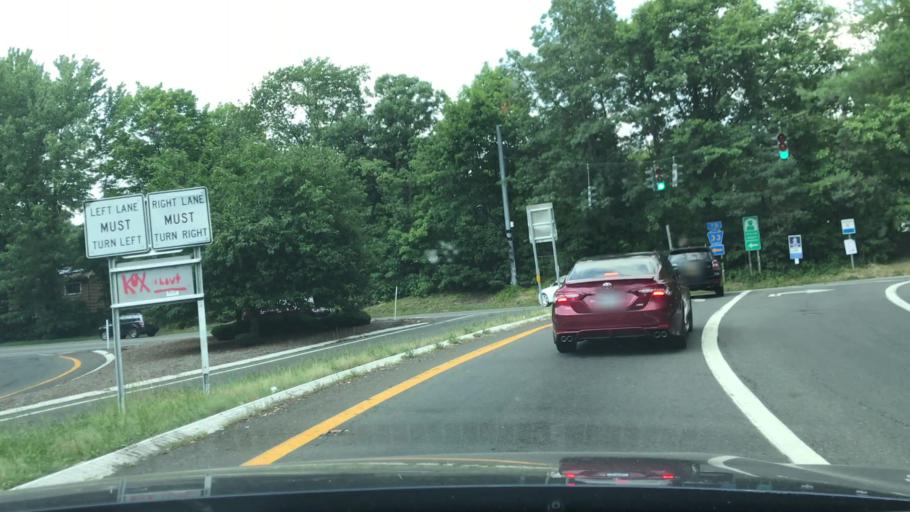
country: US
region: New York
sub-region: Rockland County
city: Bardonia
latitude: 41.1213
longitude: -74.0061
